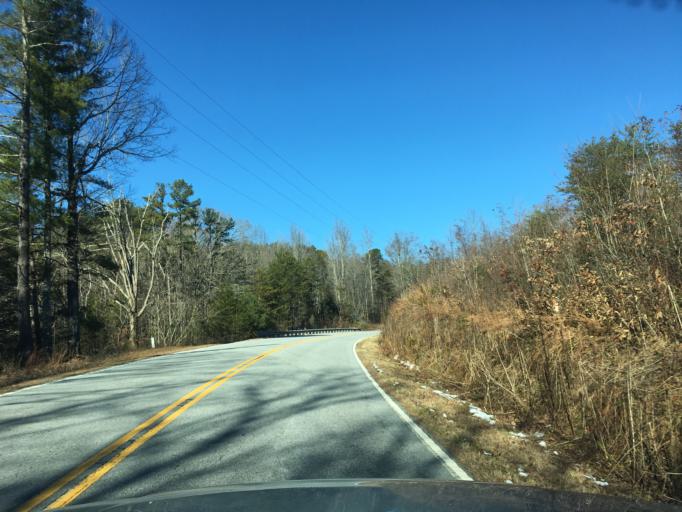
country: US
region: South Carolina
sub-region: Oconee County
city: Walhalla
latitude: 34.9156
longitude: -82.9853
